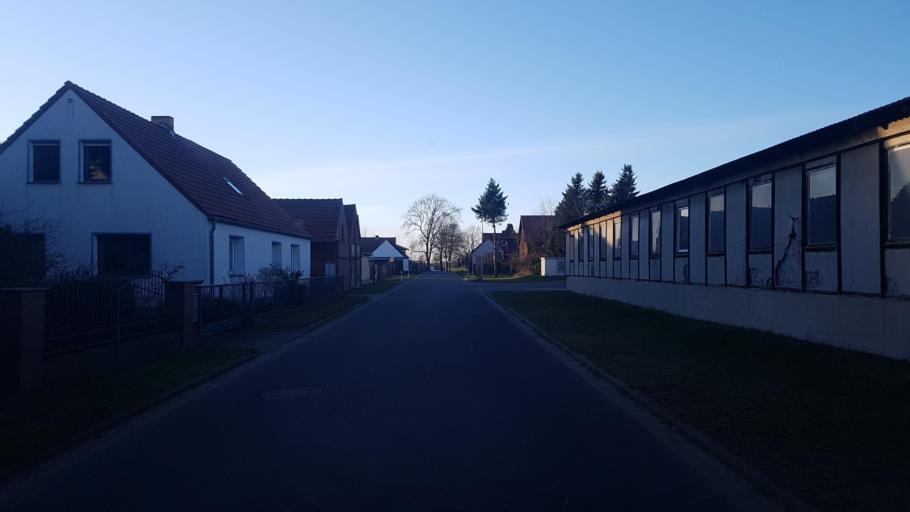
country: DE
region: Brandenburg
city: Drehnow
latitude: 51.8667
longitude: 14.3507
